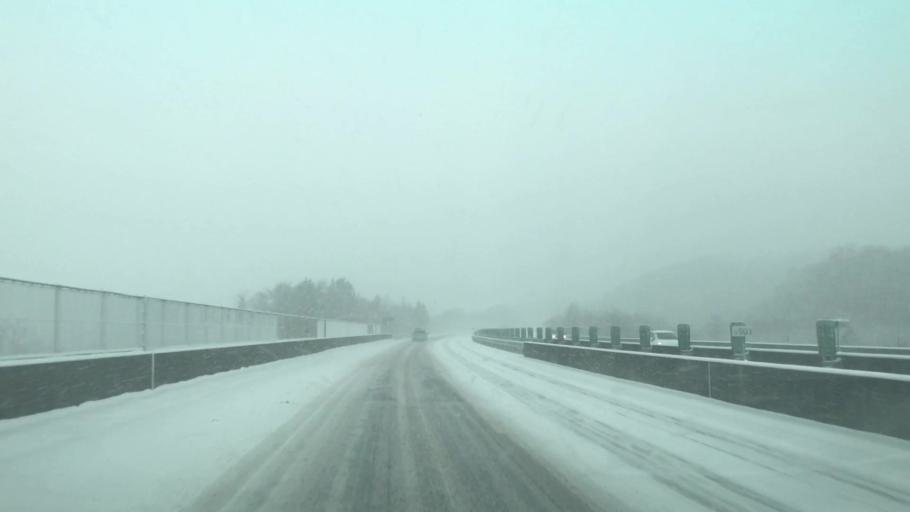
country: JP
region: Hokkaido
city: Shiraoi
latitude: 42.5013
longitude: 141.2650
